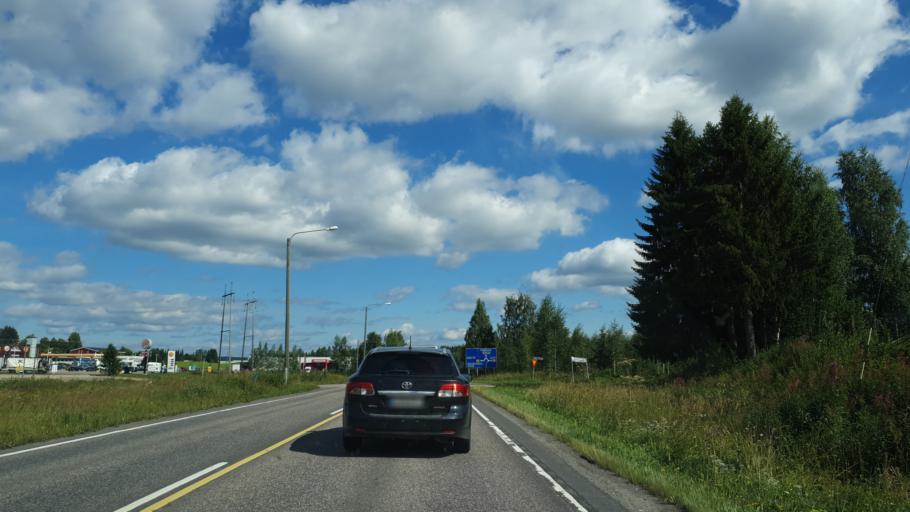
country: FI
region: Central Finland
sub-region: Jaemsae
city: Jaemsae
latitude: 61.8504
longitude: 25.1692
